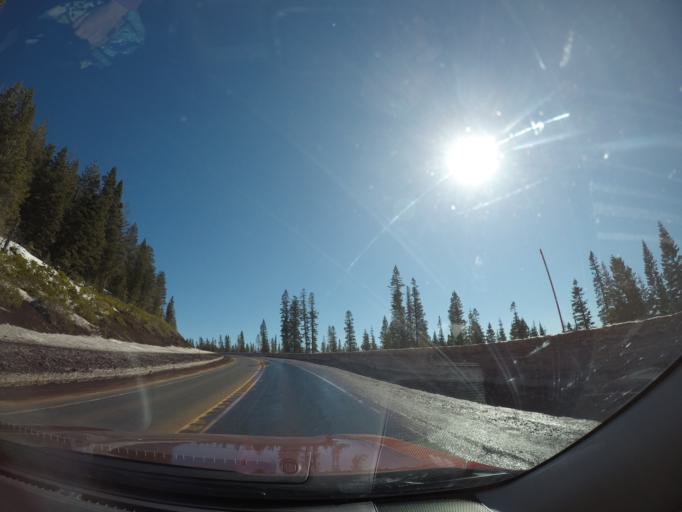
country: US
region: Oregon
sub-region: Deschutes County
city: Sunriver
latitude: 43.9805
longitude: -121.5883
